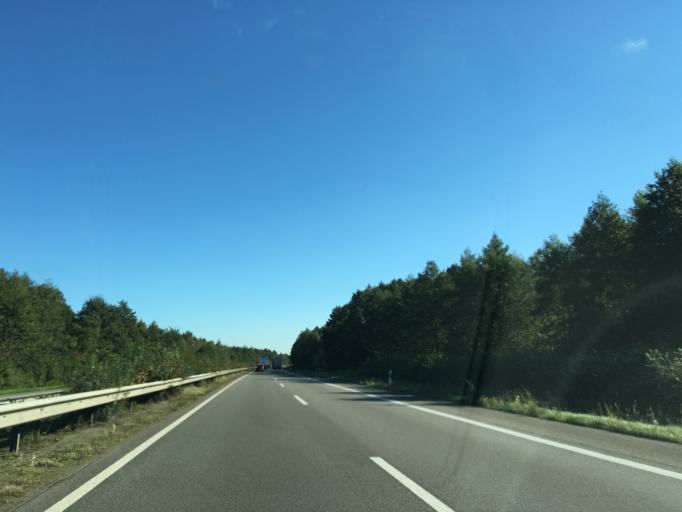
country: DE
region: Lower Saxony
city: Radbruch
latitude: 53.3286
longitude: 10.2813
